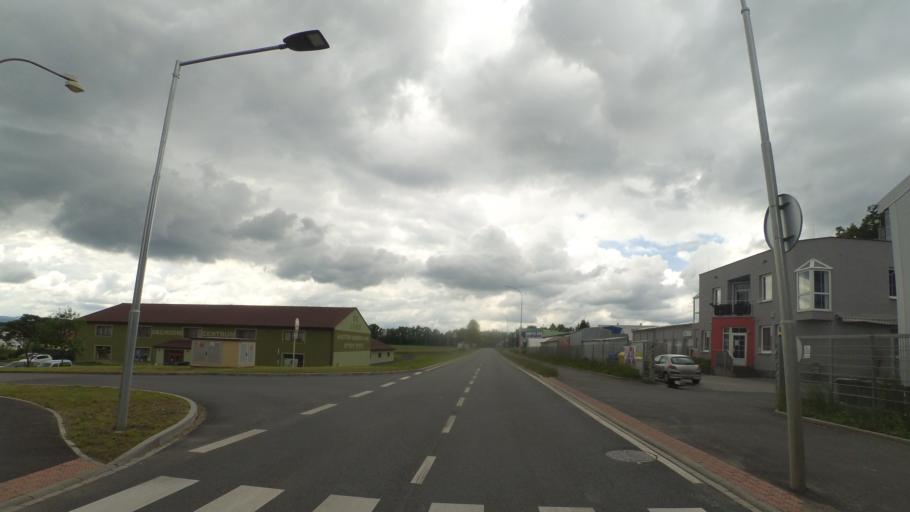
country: CZ
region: Plzensky
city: Horsovsky Tyn
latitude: 49.5340
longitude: 12.9296
